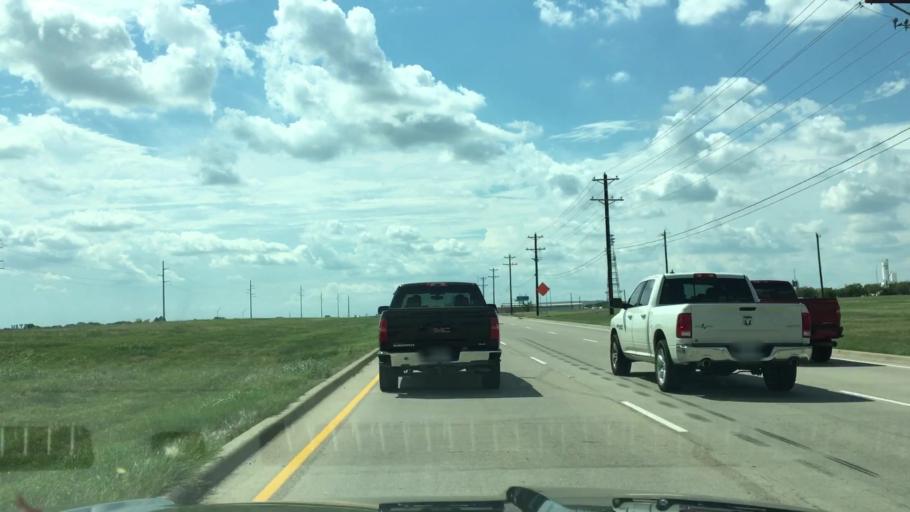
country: US
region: Texas
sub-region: Denton County
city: Justin
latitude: 33.0270
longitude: -97.2894
